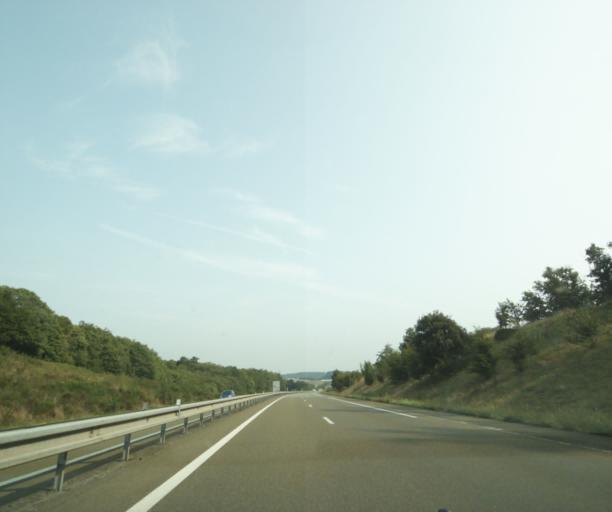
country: FR
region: Pays de la Loire
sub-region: Departement de la Sarthe
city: Neuville-sur-Sarthe
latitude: 48.0734
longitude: 0.1724
